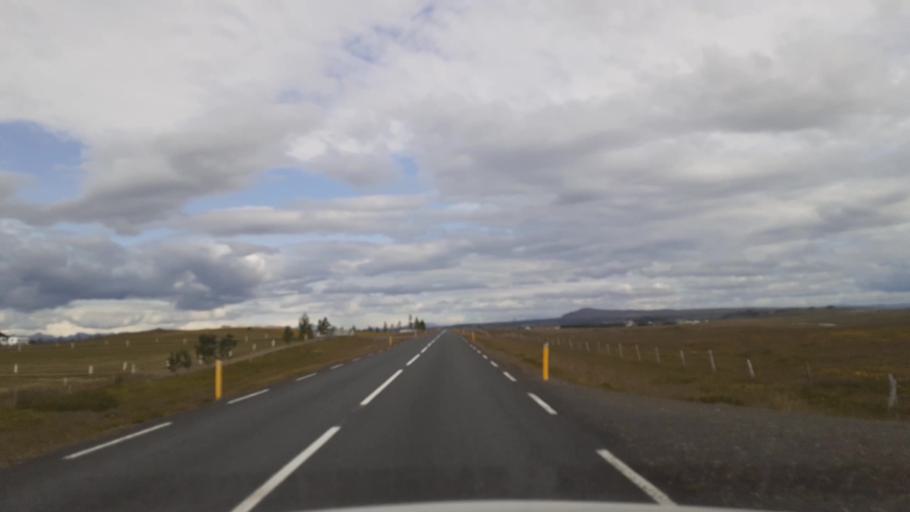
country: IS
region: South
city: Selfoss
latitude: 63.9282
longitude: -20.8482
